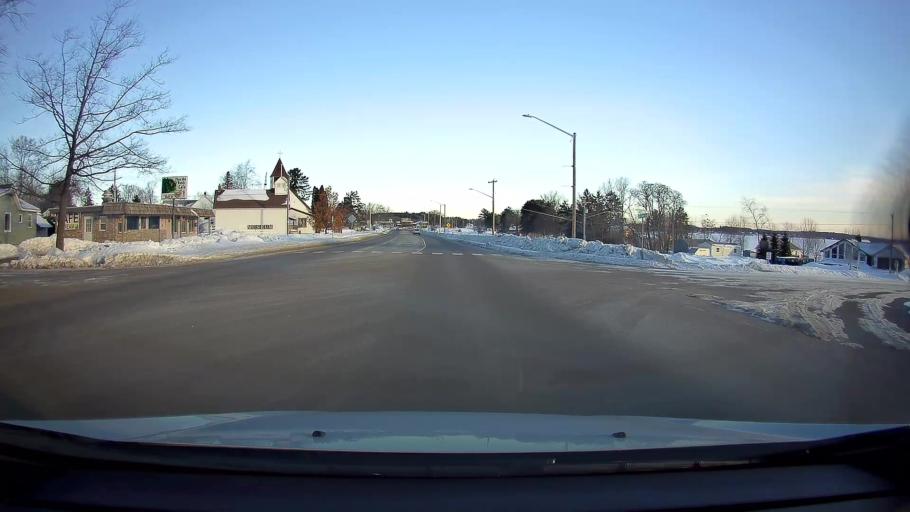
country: US
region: Wisconsin
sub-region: Washburn County
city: Shell Lake
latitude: 45.7389
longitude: -91.9260
